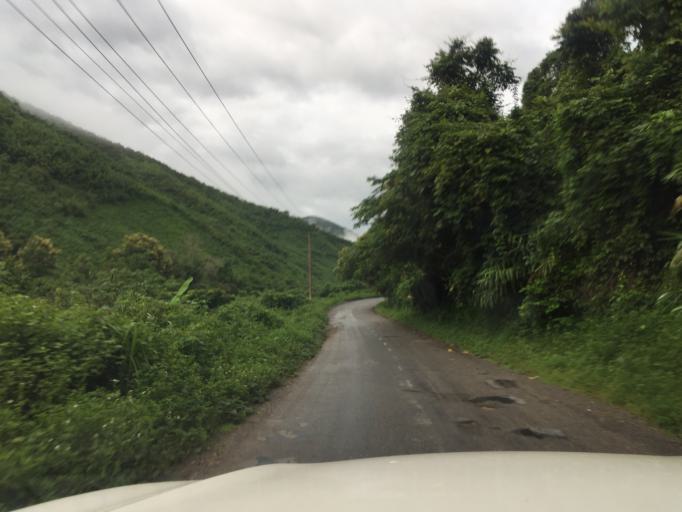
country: LA
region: Oudomxai
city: Muang La
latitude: 21.0413
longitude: 102.2414
